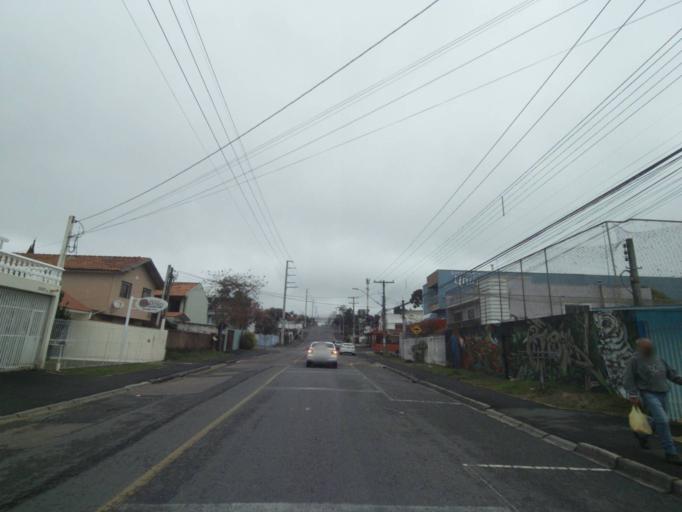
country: BR
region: Parana
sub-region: Curitiba
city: Curitiba
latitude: -25.5147
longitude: -49.3044
